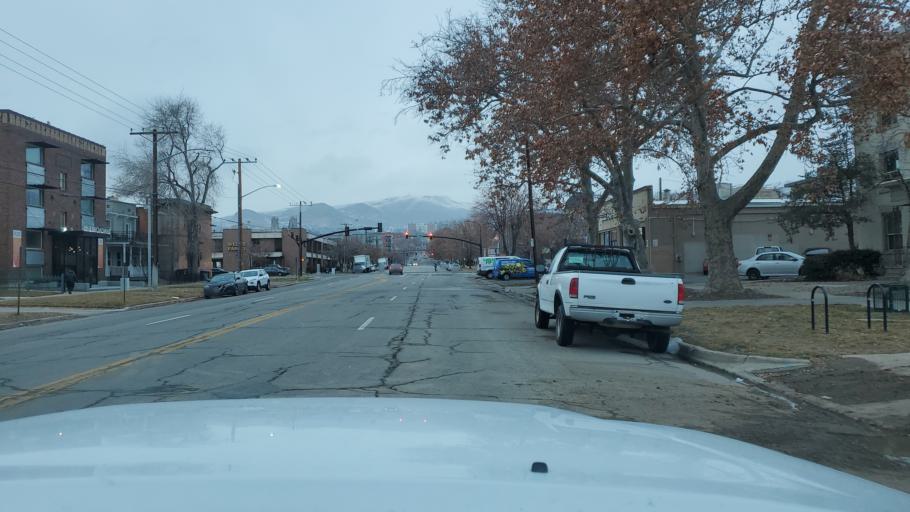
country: US
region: Utah
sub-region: Salt Lake County
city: Salt Lake City
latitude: 40.7618
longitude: -111.8796
